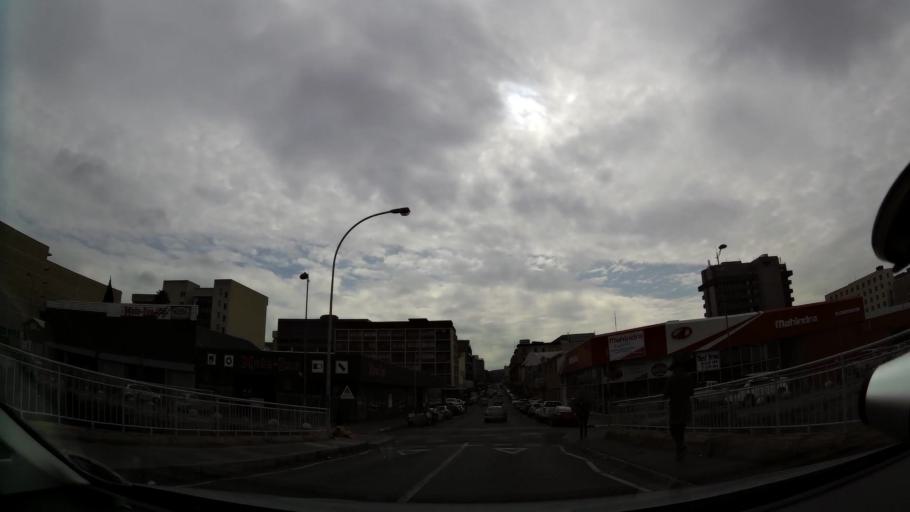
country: ZA
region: Orange Free State
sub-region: Mangaung Metropolitan Municipality
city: Bloemfontein
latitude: -29.1196
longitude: 26.2199
